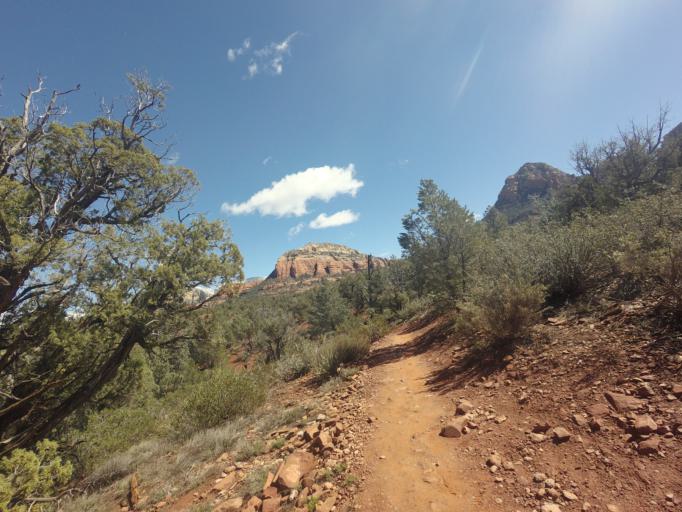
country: US
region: Arizona
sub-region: Yavapai County
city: West Sedona
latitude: 34.9007
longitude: -111.8226
